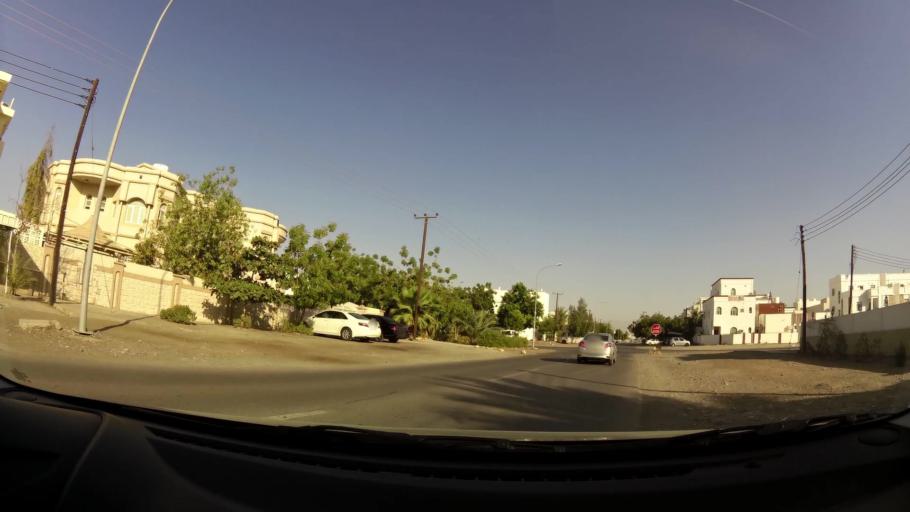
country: OM
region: Muhafazat Masqat
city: As Sib al Jadidah
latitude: 23.6337
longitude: 58.2058
